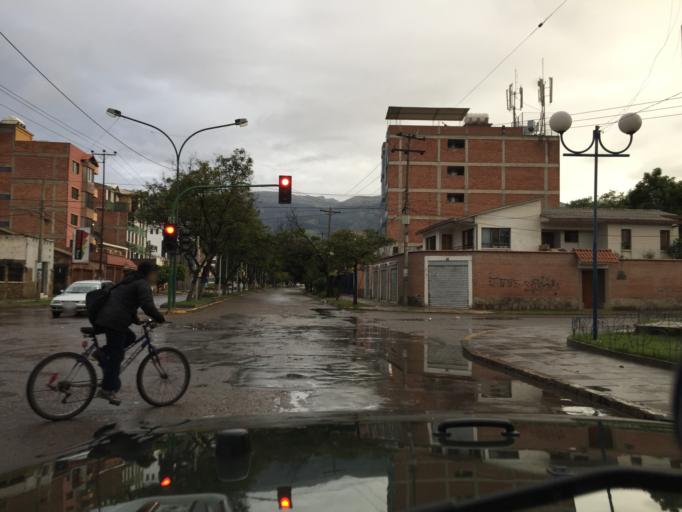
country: BO
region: Cochabamba
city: Cochabamba
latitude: -17.3909
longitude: -66.1669
